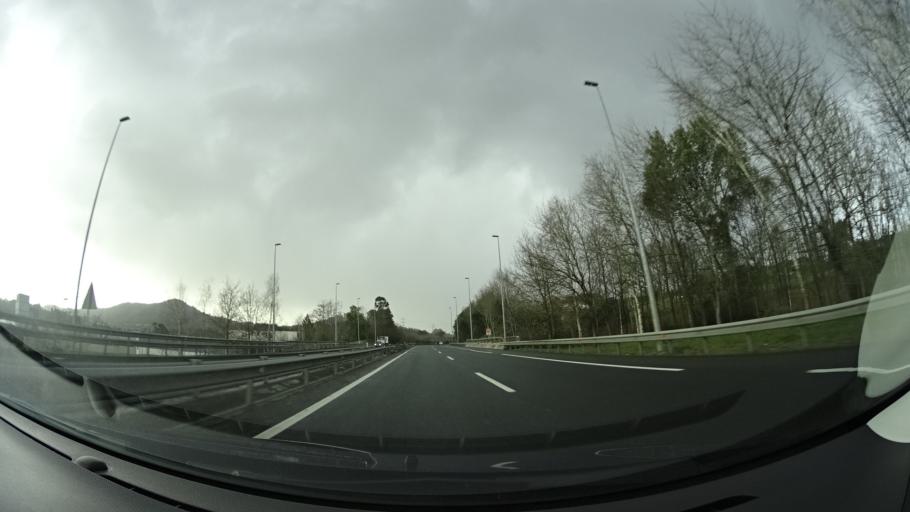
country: ES
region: Basque Country
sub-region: Bizkaia
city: Gatika
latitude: 43.3406
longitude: -2.8642
